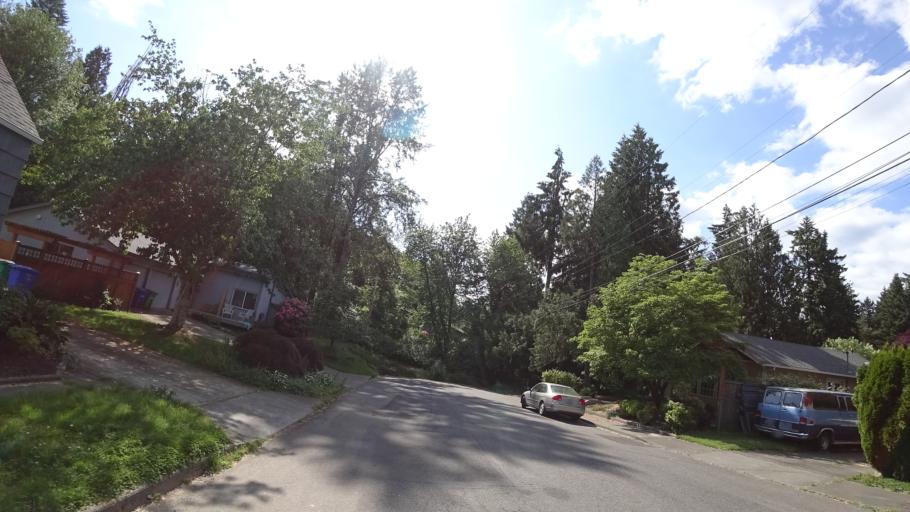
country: US
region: Oregon
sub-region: Washington County
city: Garden Home-Whitford
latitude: 45.4703
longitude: -122.7149
